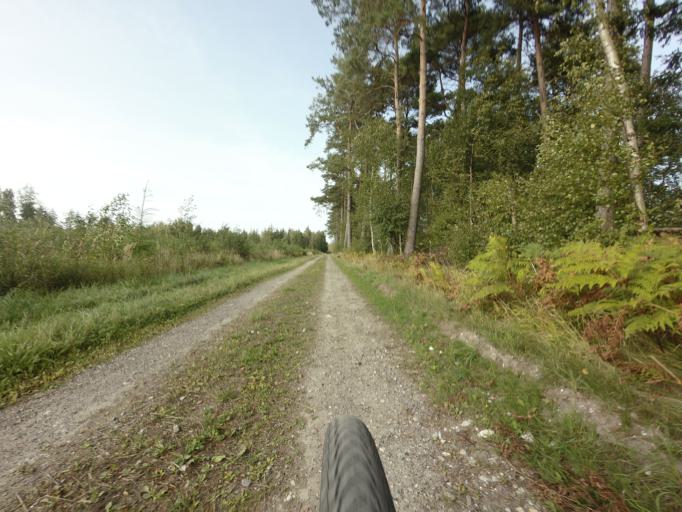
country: DK
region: Zealand
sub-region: Vordingborg Kommune
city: Praesto
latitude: 55.1482
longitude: 12.0990
